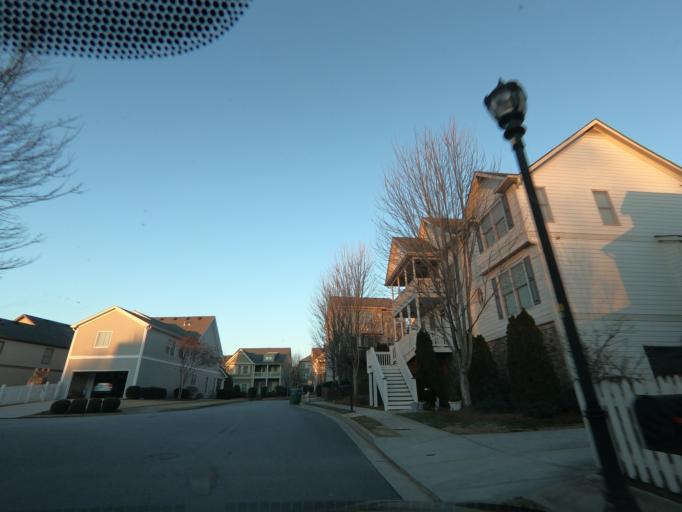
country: US
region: Georgia
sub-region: Cobb County
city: Vinings
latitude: 33.8092
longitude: -84.4501
